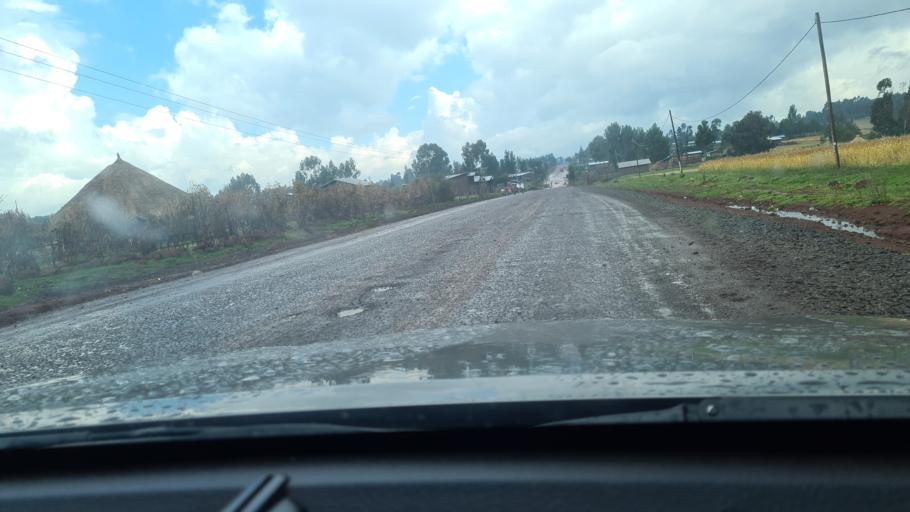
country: ET
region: Oromiya
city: Huruta
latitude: 8.0726
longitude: 39.5496
